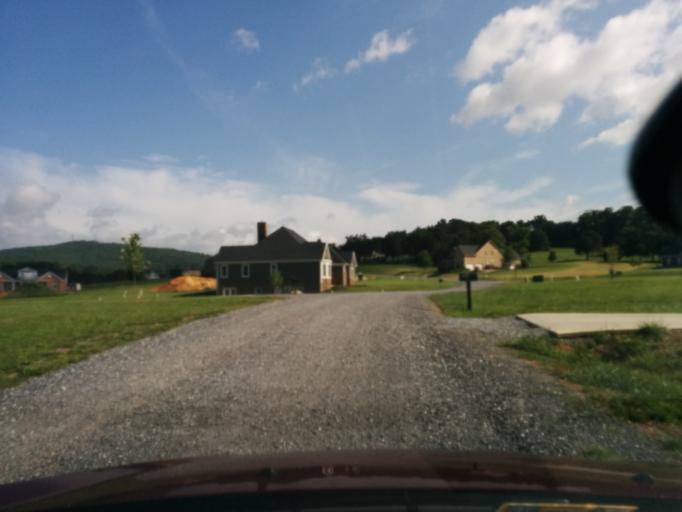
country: US
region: Virginia
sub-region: City of Lexington
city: Lexington
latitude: 37.7684
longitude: -79.4702
